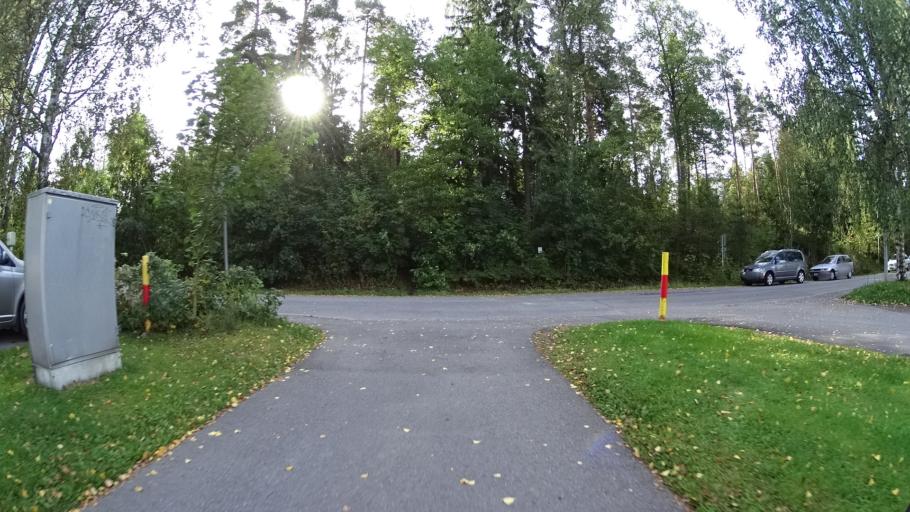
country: FI
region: Uusimaa
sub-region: Helsinki
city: Kilo
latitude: 60.2283
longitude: 24.7752
